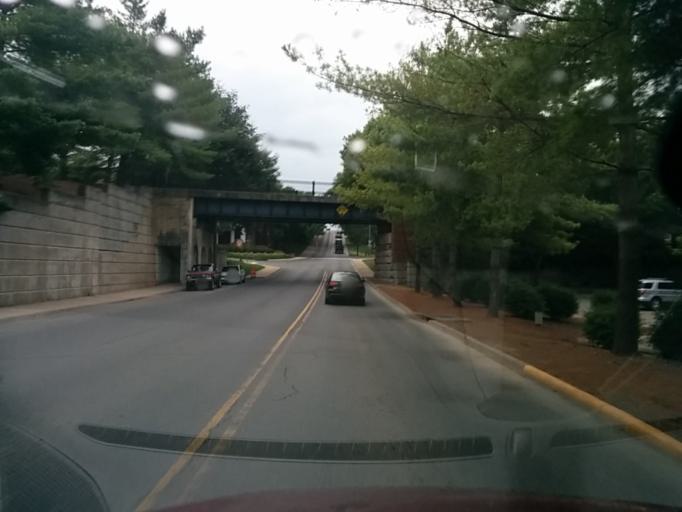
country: US
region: Virginia
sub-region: City of Lexington
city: Lexington
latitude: 37.7875
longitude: -79.4475
